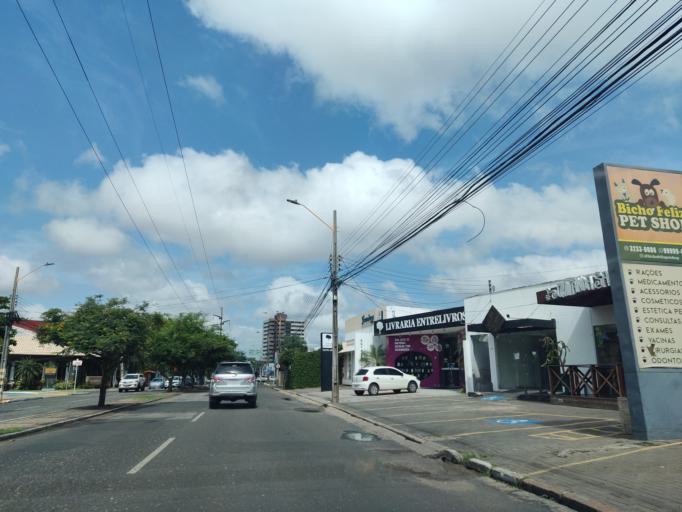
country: BR
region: Piaui
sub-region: Teresina
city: Teresina
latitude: -5.0699
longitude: -42.7909
